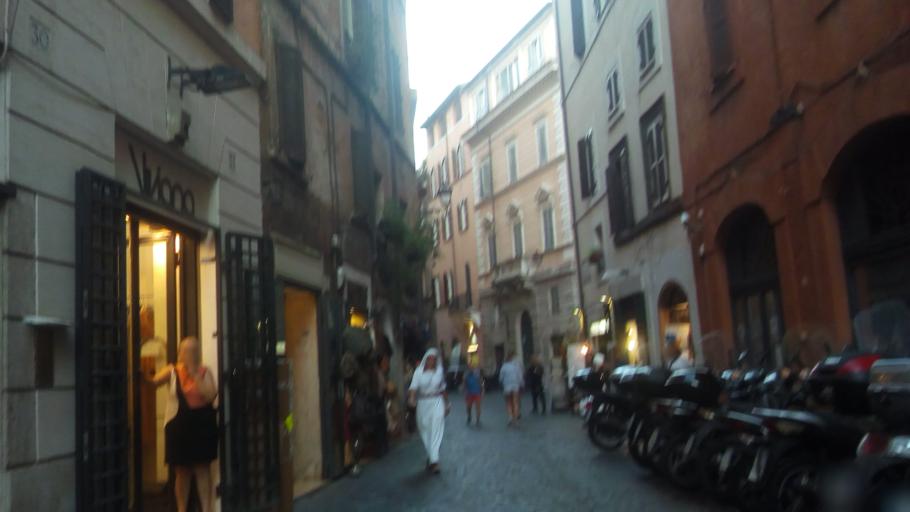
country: VA
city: Vatican City
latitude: 41.8987
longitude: 12.4693
